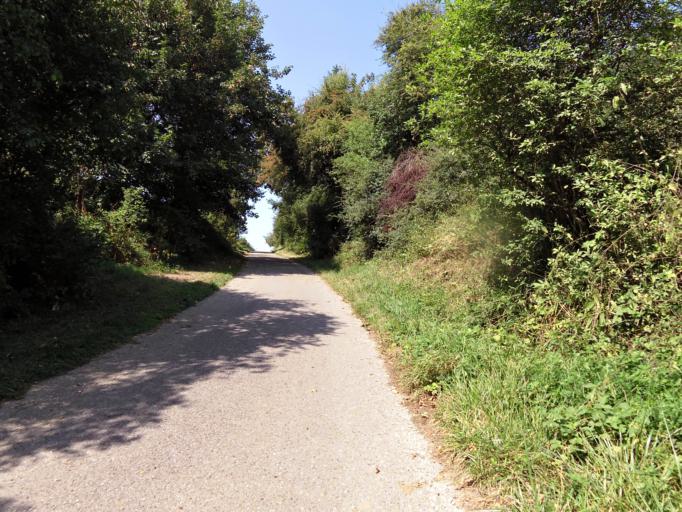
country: DE
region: Baden-Wuerttemberg
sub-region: Karlsruhe Region
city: Neidenstein
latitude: 49.3095
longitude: 8.8968
